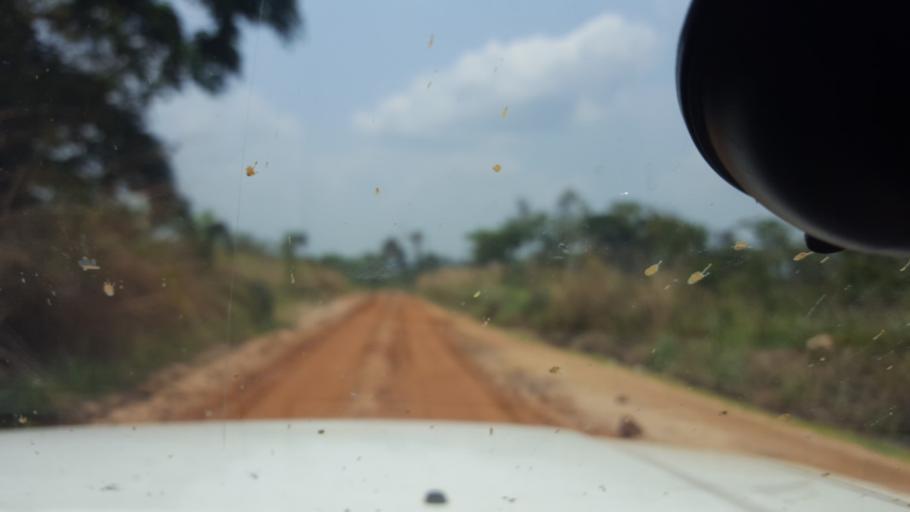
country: CD
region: Bandundu
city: Mushie
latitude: -3.7504
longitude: 16.6349
